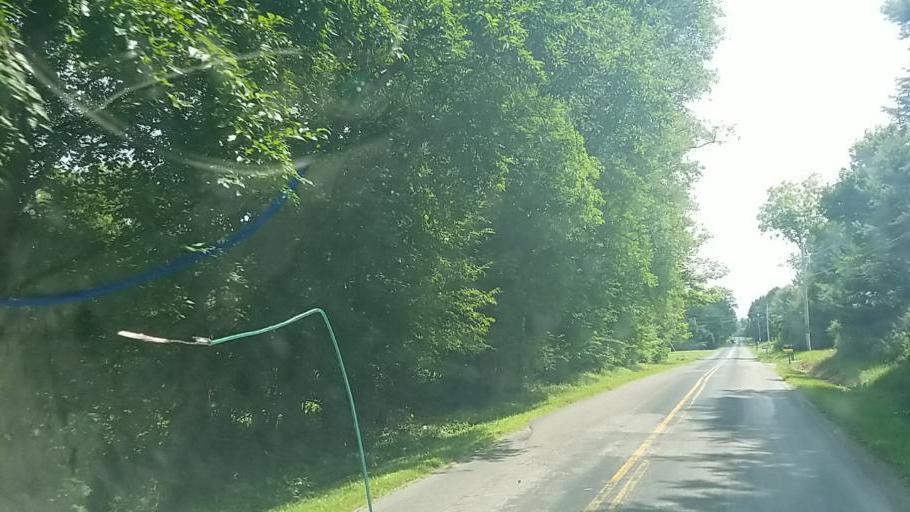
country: US
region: Ohio
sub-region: Medina County
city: Lodi
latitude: 41.0141
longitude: -82.0639
